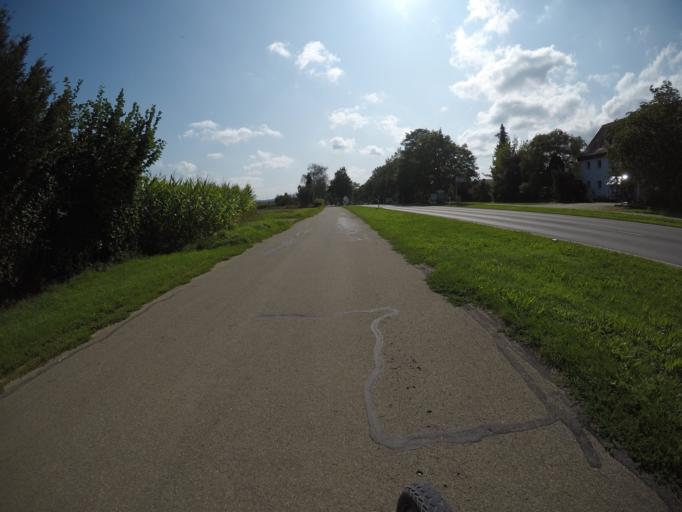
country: DE
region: Baden-Wuerttemberg
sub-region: Regierungsbezirk Stuttgart
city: Kongen
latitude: 48.6836
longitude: 9.3556
